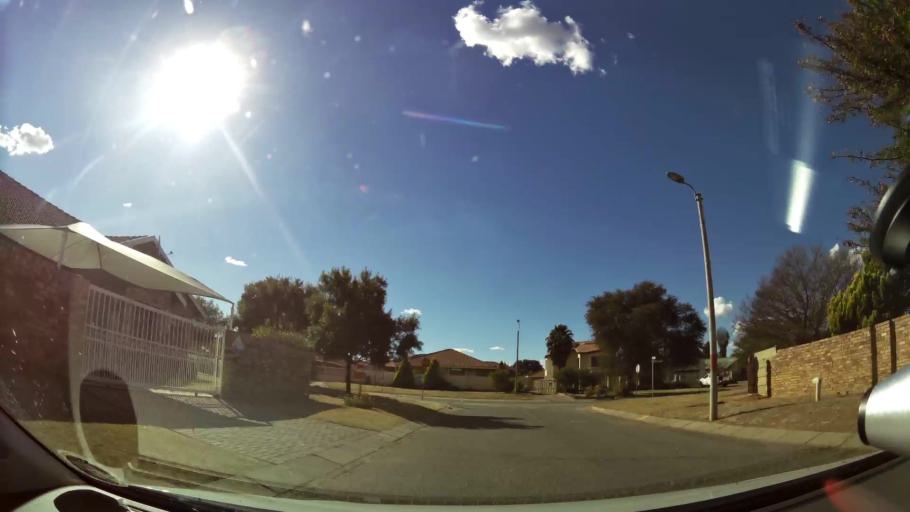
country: ZA
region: North-West
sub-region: Dr Kenneth Kaunda District Municipality
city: Klerksdorp
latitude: -26.8338
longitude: 26.6535
